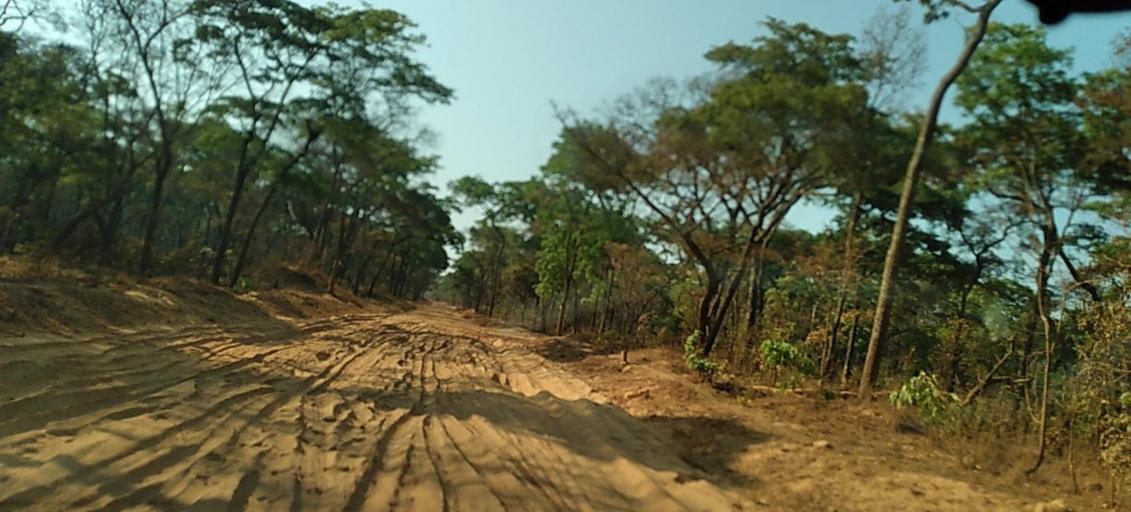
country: ZM
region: North-Western
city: Kasempa
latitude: -13.6304
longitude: 25.9881
